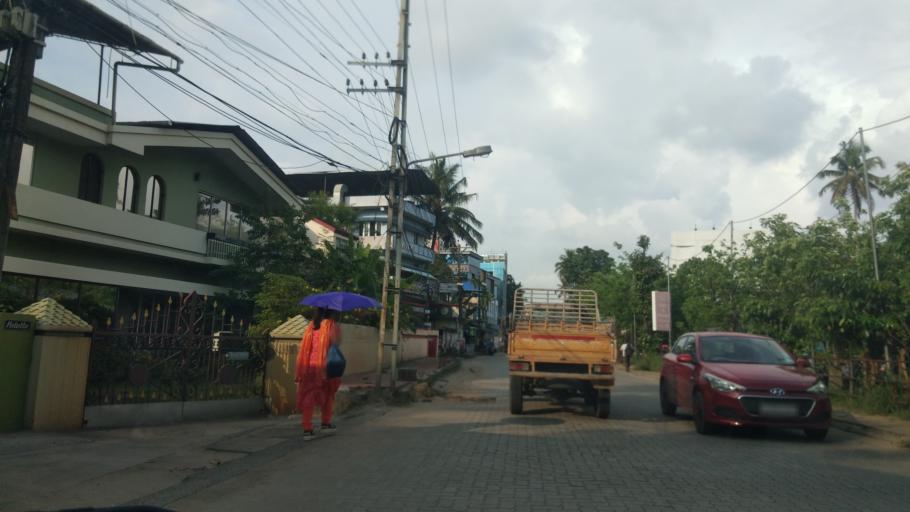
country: IN
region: Kerala
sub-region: Ernakulam
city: Cochin
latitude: 9.9694
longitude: 76.3201
